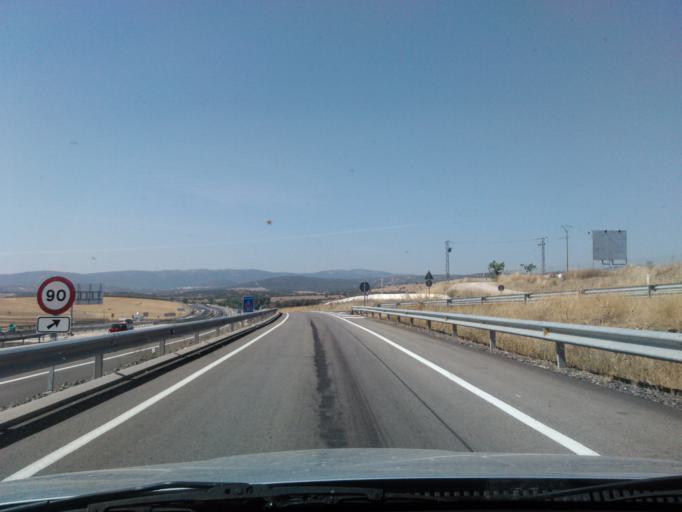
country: ES
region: Castille-La Mancha
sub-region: Provincia de Ciudad Real
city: Viso del Marques
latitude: 38.5055
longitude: -3.4995
